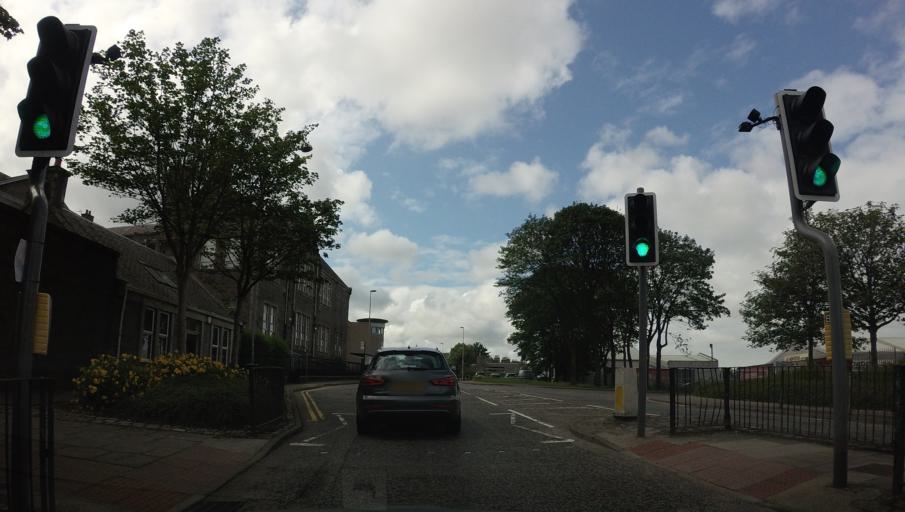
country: GB
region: Scotland
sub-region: Aberdeen City
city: Aberdeen
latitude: 57.1517
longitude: -2.1093
